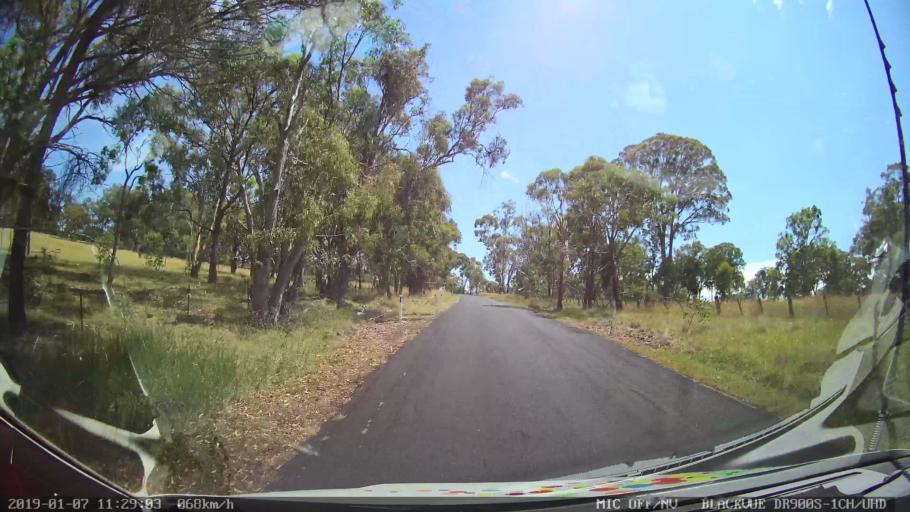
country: AU
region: New South Wales
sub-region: Armidale Dumaresq
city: Armidale
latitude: -30.4425
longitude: 151.5648
